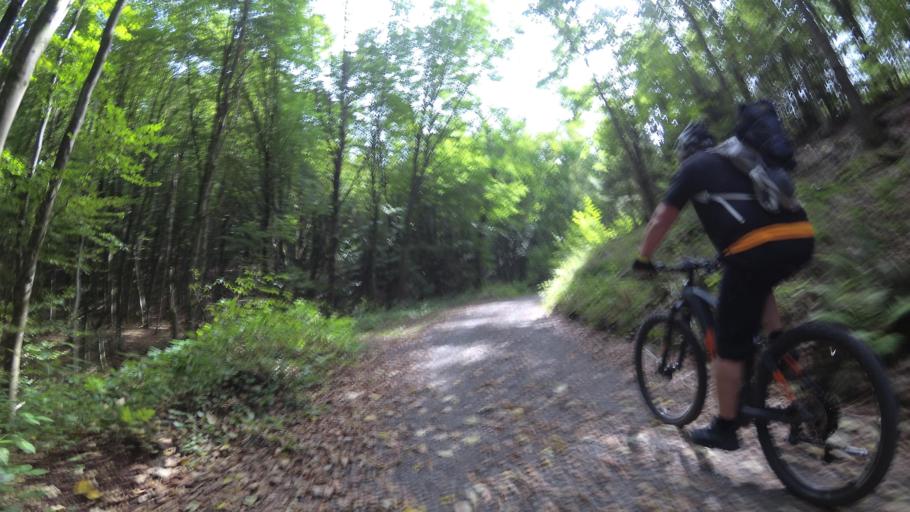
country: DE
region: Saarland
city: Friedrichsthal
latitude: 49.3032
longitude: 7.1045
